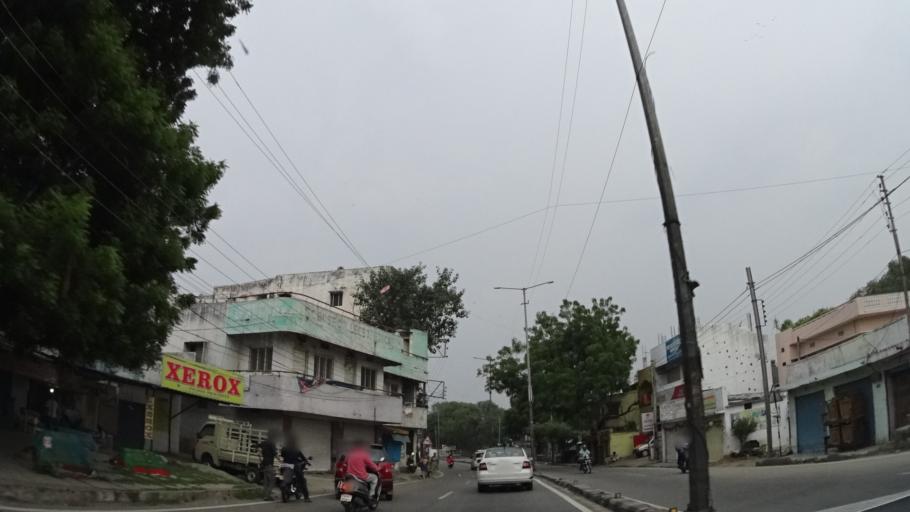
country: IN
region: Telangana
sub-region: Rangareddi
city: Quthbullapur
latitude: 17.4609
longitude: 78.4757
